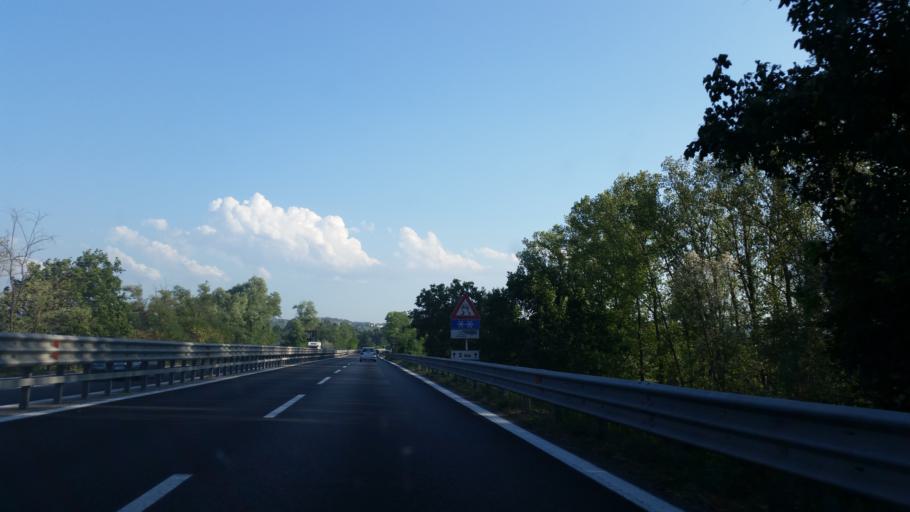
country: IT
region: Piedmont
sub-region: Provincia di Asti
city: Azzano d'Asti
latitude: 44.9022
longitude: 8.2461
